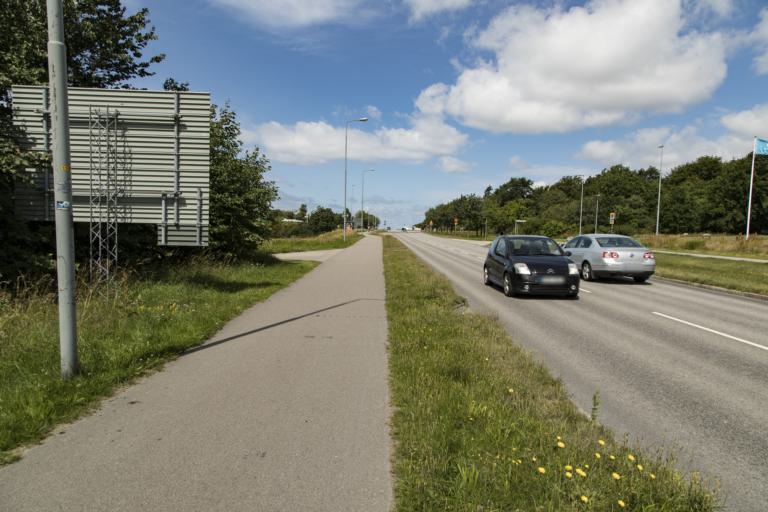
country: SE
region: Halland
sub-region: Varbergs Kommun
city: Varberg
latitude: 57.0910
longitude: 12.2630
